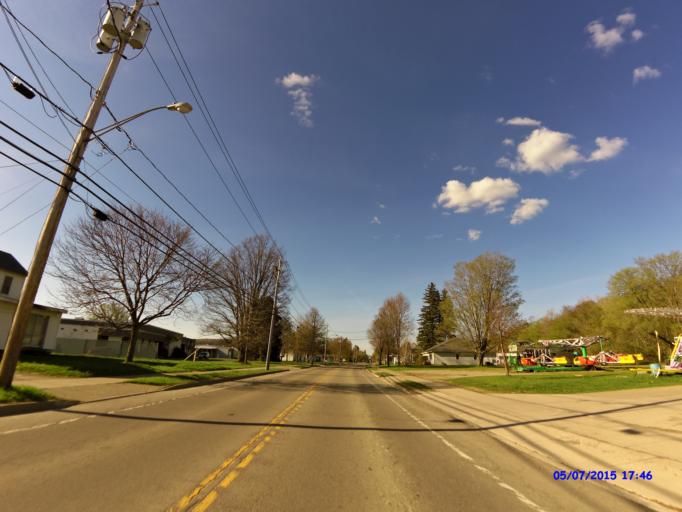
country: US
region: New York
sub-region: Cattaraugus County
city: Franklinville
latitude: 42.3285
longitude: -78.4608
